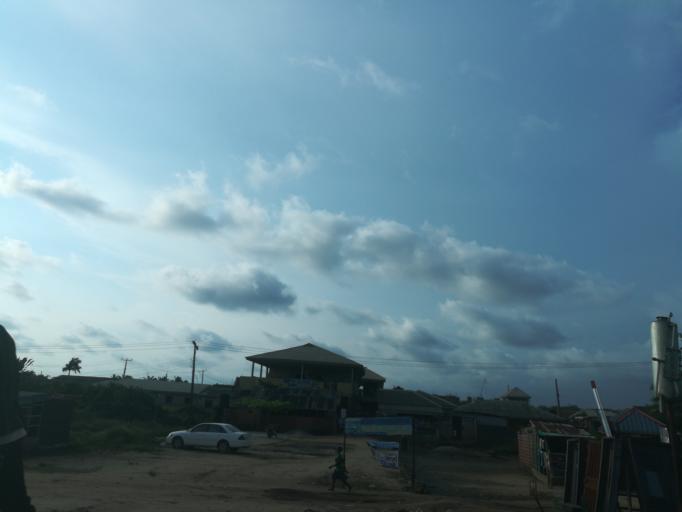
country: NG
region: Ogun
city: Ado Odo
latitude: 6.4761
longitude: 3.0208
